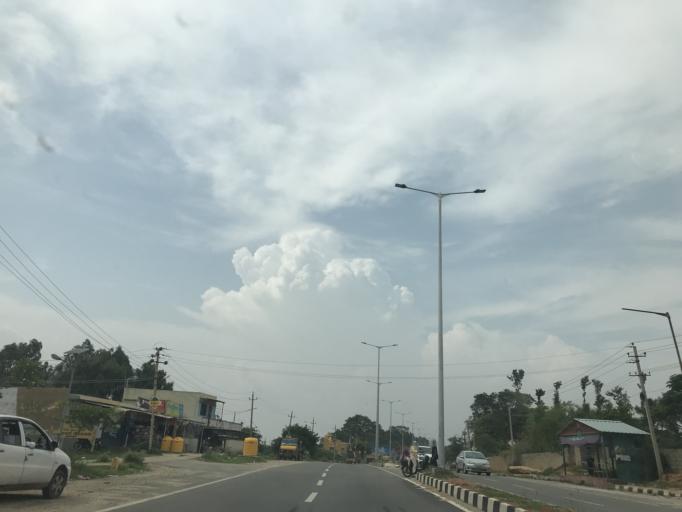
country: IN
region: Karnataka
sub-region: Bangalore Urban
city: Yelahanka
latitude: 13.1038
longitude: 77.6595
